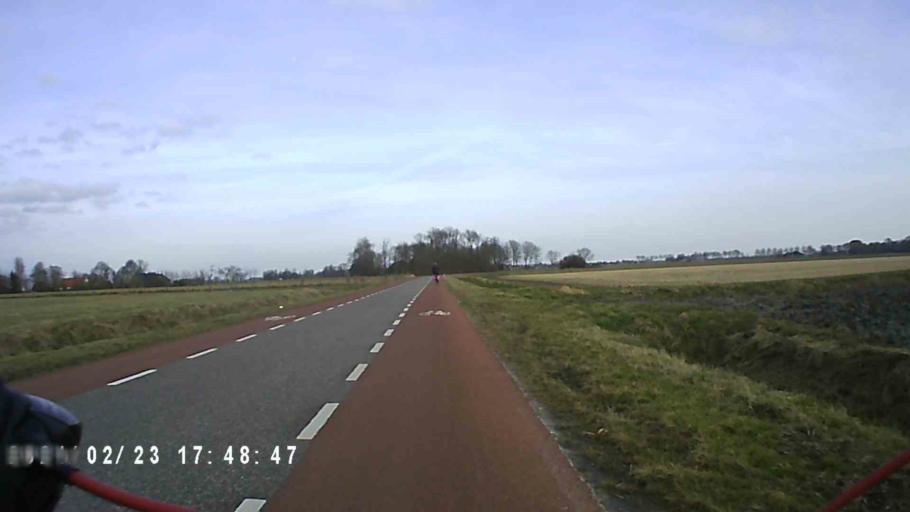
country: NL
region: Groningen
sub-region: Gemeente Winsum
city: Winsum
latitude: 53.3932
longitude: 6.5288
